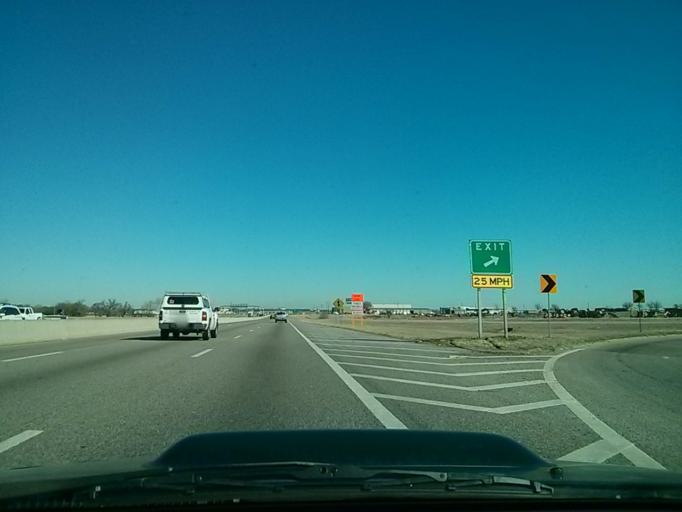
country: US
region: Oklahoma
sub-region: Tulsa County
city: Owasso
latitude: 36.2069
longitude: -95.8519
